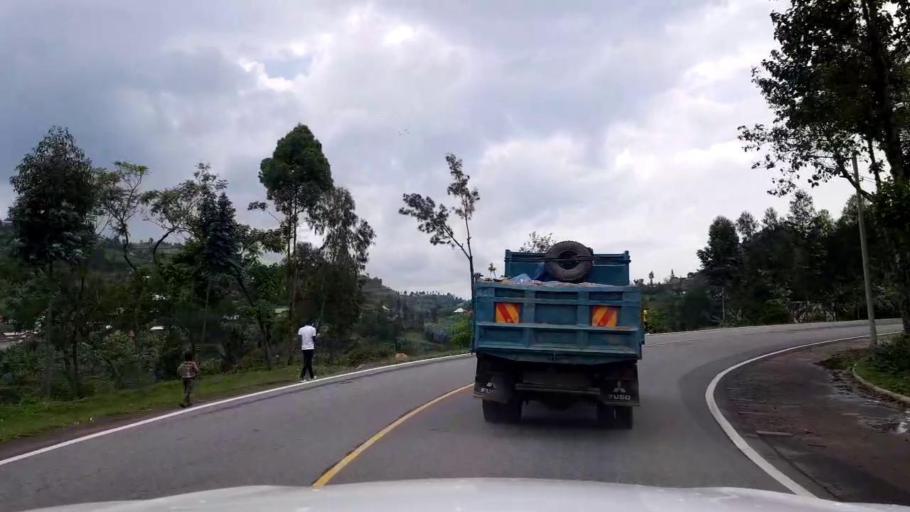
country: RW
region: Western Province
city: Gisenyi
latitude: -1.6988
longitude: 29.2718
